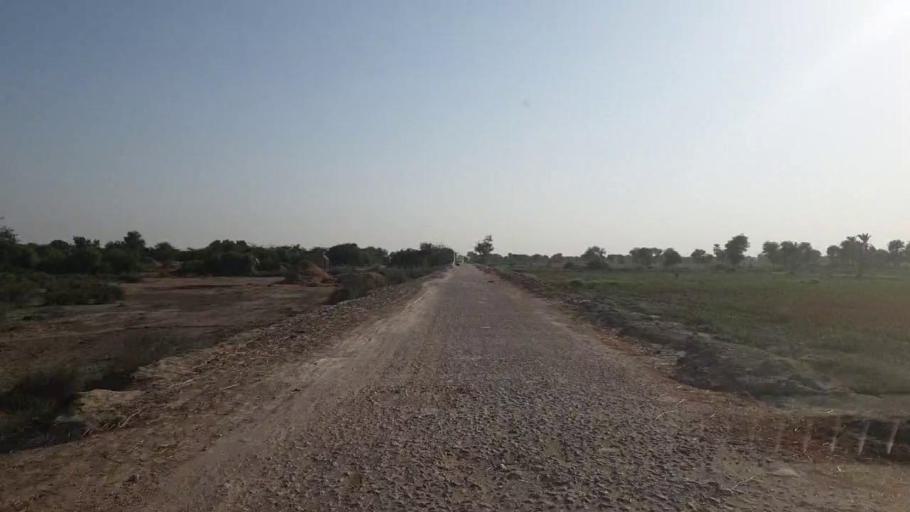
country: PK
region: Sindh
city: Talhar
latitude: 24.9348
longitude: 68.7502
